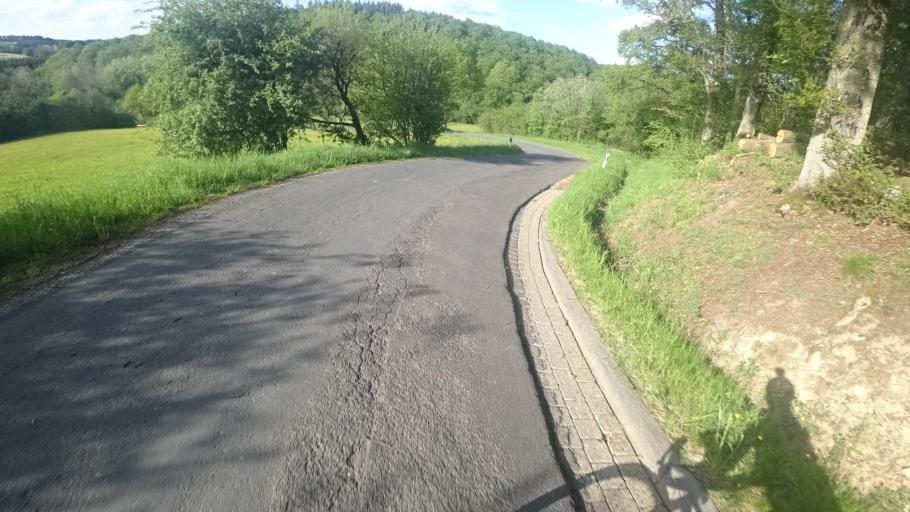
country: DE
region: Rheinland-Pfalz
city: Berg
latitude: 50.5453
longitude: 6.9634
